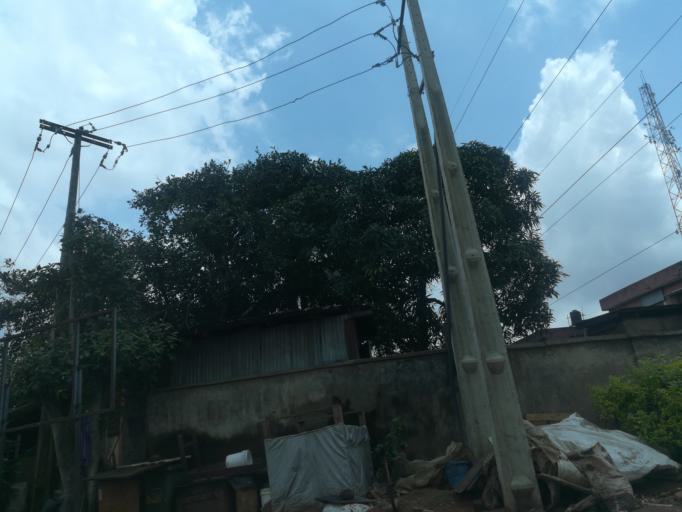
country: NG
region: Lagos
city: Somolu
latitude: 6.5530
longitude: 3.3588
